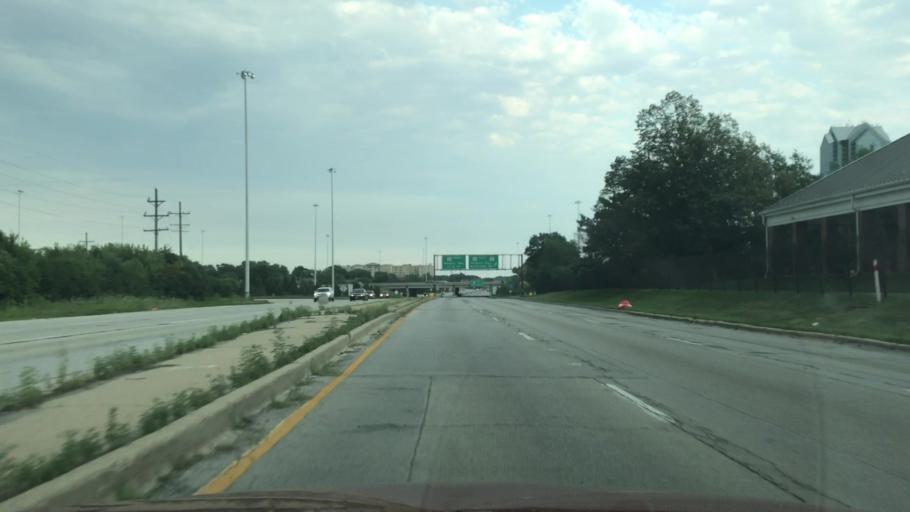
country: US
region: Illinois
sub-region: DuPage County
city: Oakbrook Terrace
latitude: 41.8608
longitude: -87.9637
